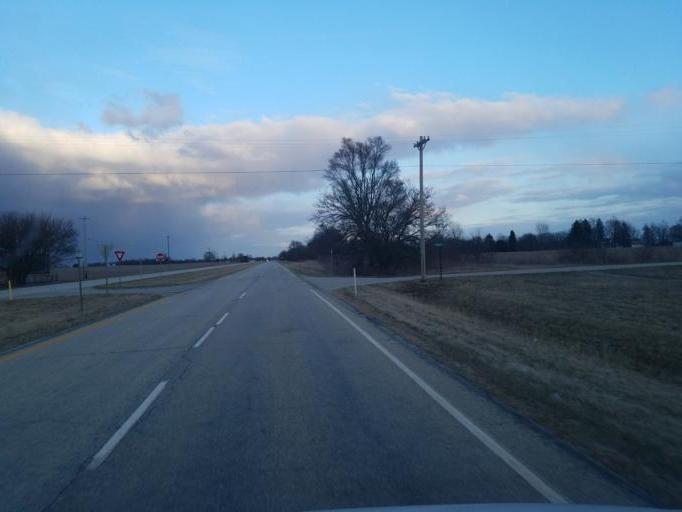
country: US
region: Indiana
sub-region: Henry County
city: Knightstown
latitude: 39.8021
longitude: -85.4620
